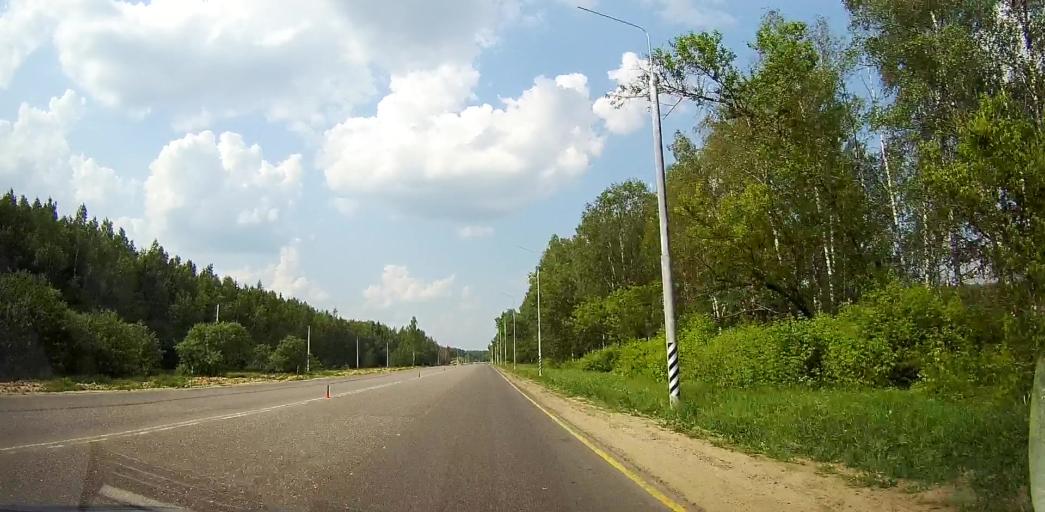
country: RU
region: Moskovskaya
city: Mikhnevo
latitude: 55.0660
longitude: 37.9533
